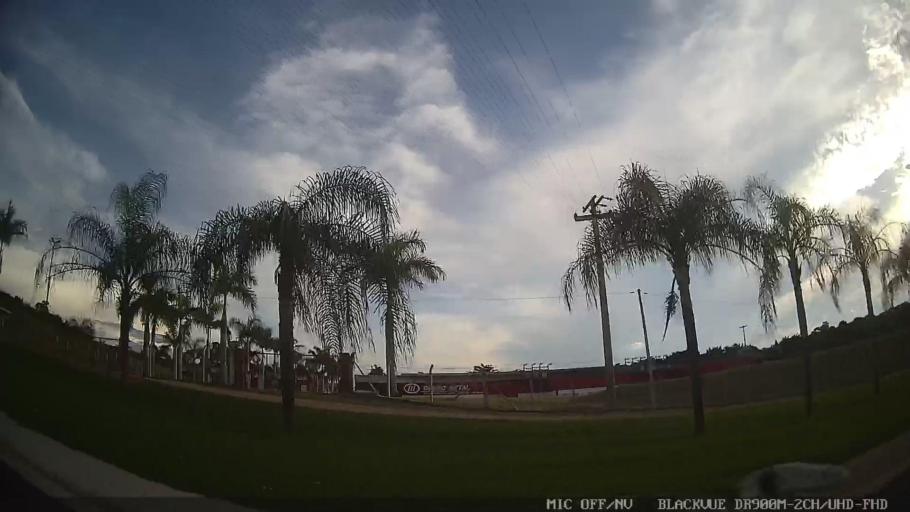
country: BR
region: Sao Paulo
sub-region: Tiete
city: Tiete
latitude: -23.1192
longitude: -47.7064
